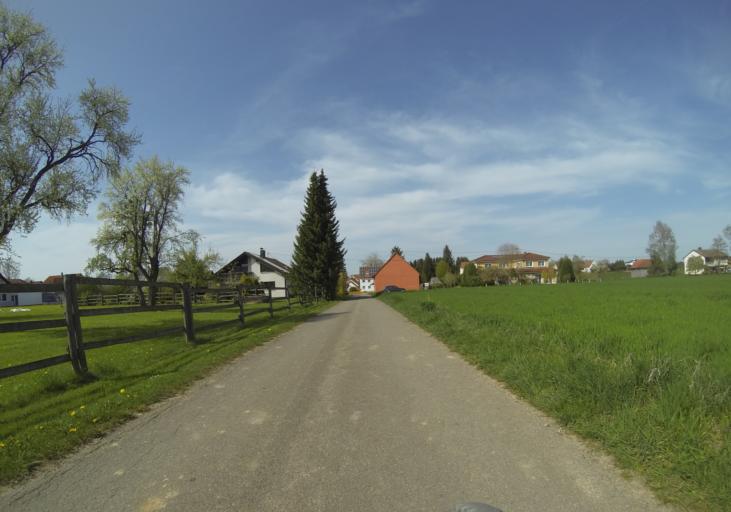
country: DE
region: Baden-Wuerttemberg
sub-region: Tuebingen Region
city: Burgrieden
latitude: 48.2580
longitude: 9.9281
